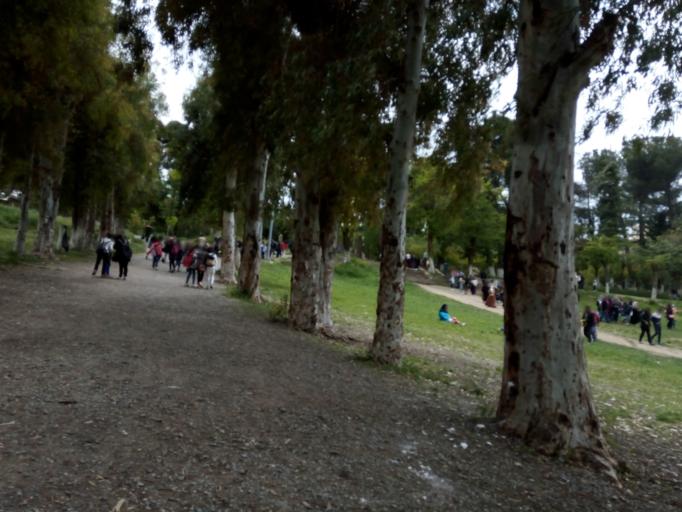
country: DZ
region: Setif
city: El Eulma
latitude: 36.3176
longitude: 5.7375
